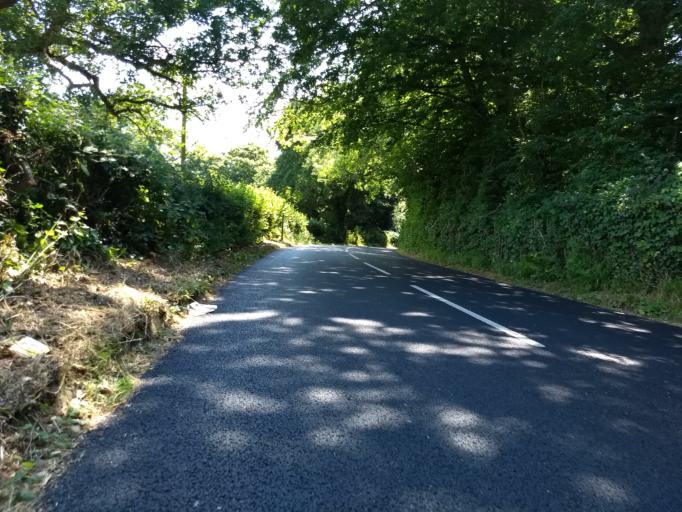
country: GB
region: England
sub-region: Isle of Wight
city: Bembridge
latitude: 50.6808
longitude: -1.0887
